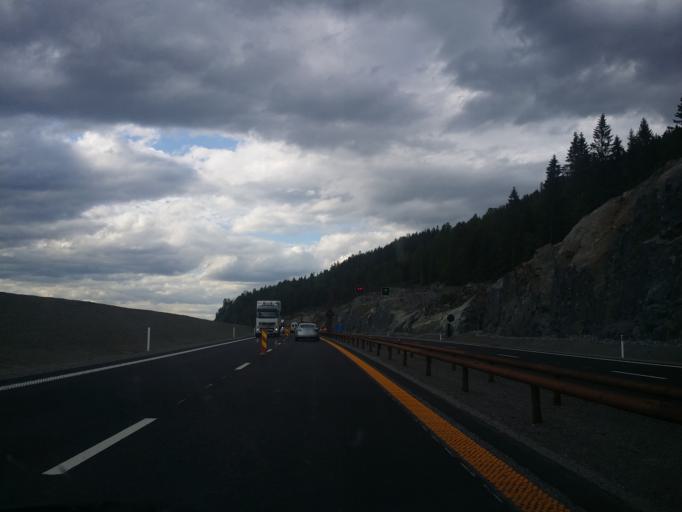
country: NO
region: Akershus
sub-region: Eidsvoll
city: Eidsvoll
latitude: 60.4285
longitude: 11.2410
